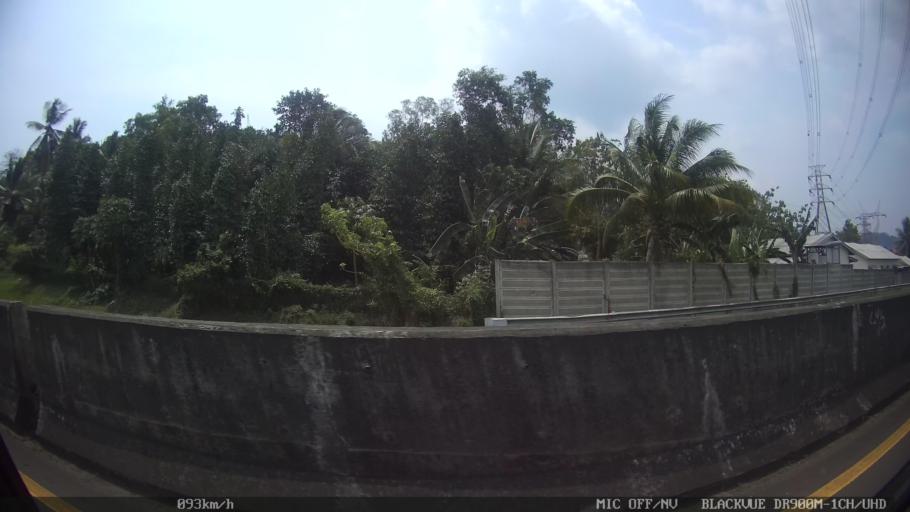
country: ID
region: Banten
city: Curug
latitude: -5.9828
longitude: 106.0257
